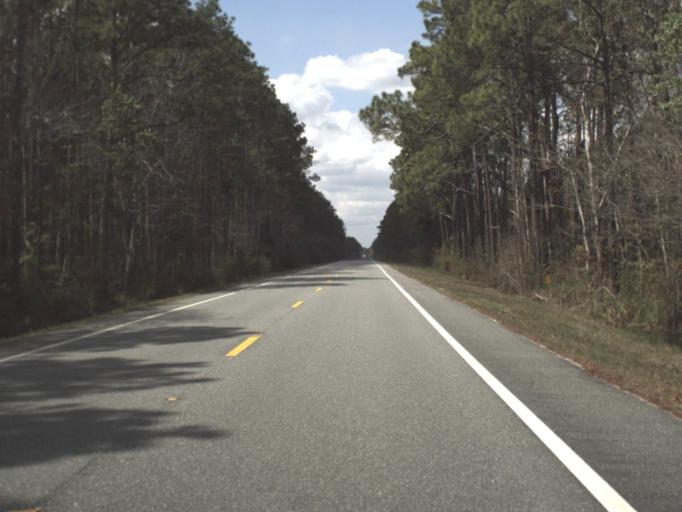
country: US
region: Florida
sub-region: Franklin County
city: Apalachicola
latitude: 29.8403
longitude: -84.9442
